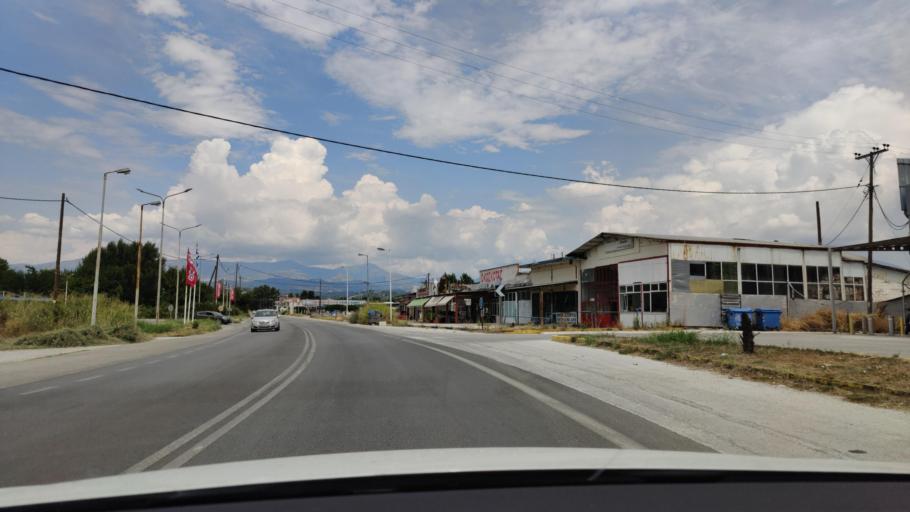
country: GR
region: Central Macedonia
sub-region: Nomos Serron
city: Serres
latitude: 41.0639
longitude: 23.5401
